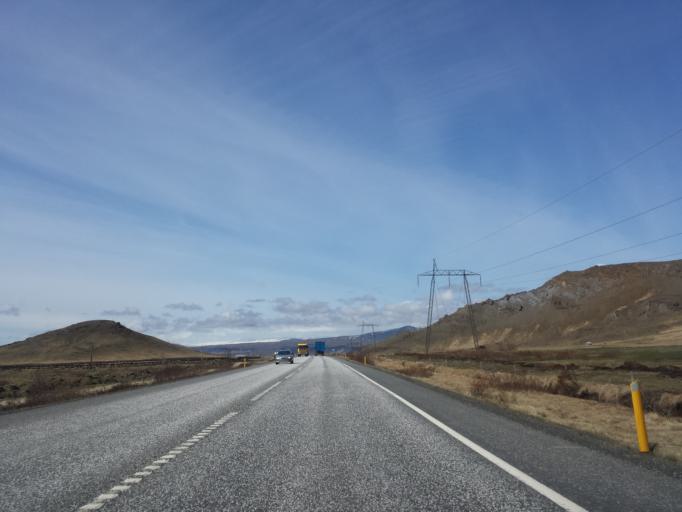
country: IS
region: South
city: Selfoss
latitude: 63.9573
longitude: -21.0647
